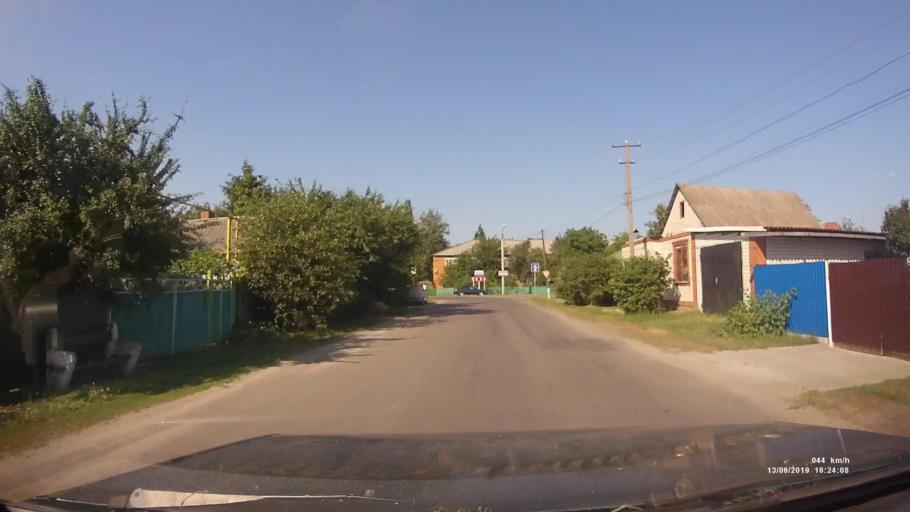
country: RU
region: Rostov
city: Kazanskaya
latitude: 49.7972
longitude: 41.1454
